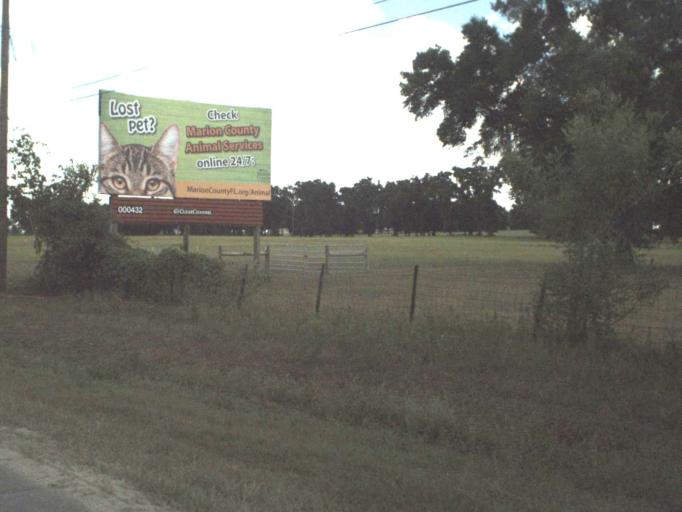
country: US
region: Florida
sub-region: Marion County
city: Belleview
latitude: 29.0731
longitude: -82.0535
